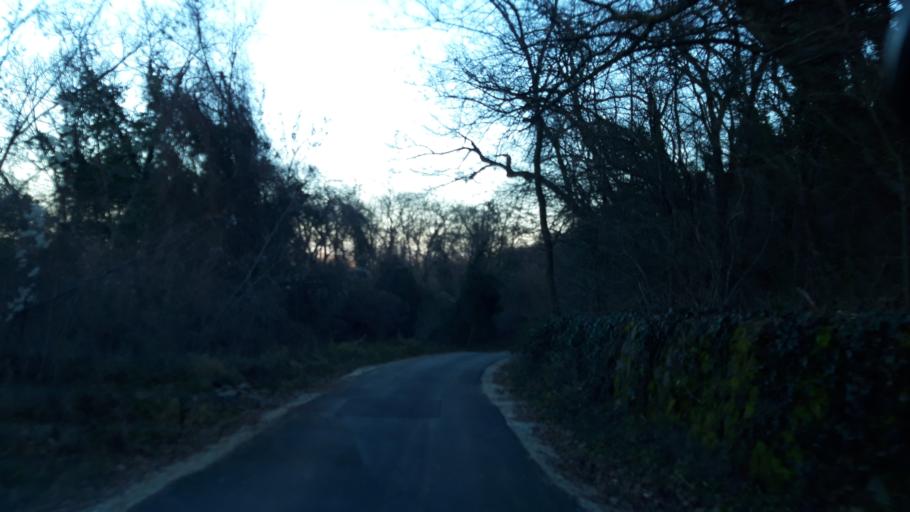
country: RS
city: Cortanovci
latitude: 45.1668
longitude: 20.0020
